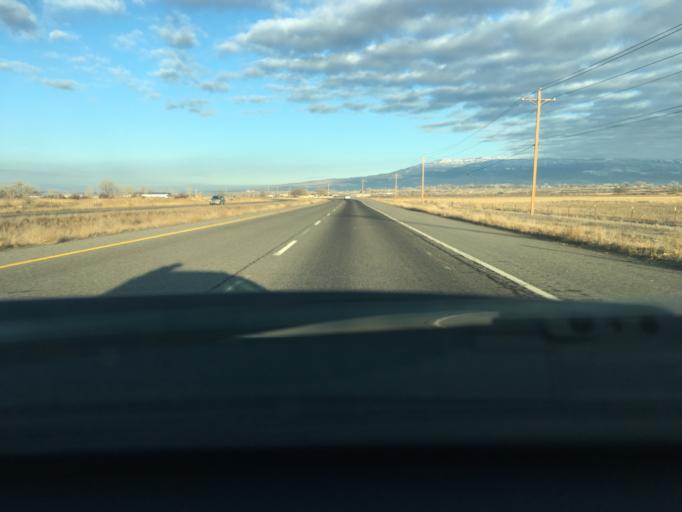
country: US
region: Colorado
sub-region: Delta County
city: Delta
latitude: 38.6918
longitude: -108.0167
